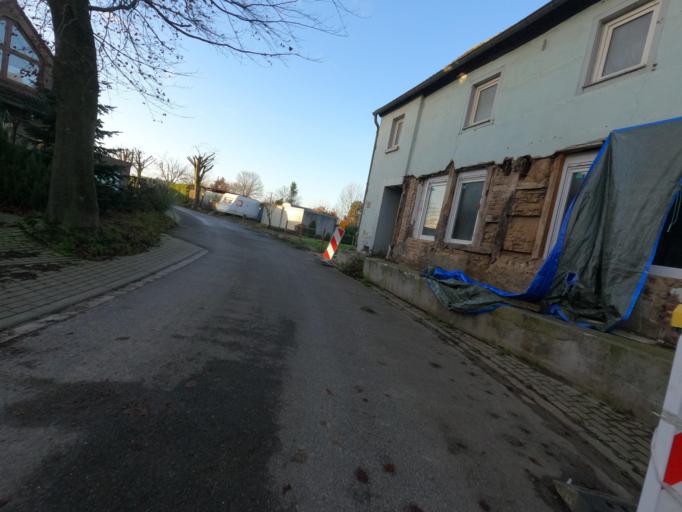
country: DE
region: North Rhine-Westphalia
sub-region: Regierungsbezirk Koln
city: Titz
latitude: 50.9876
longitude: 6.3896
